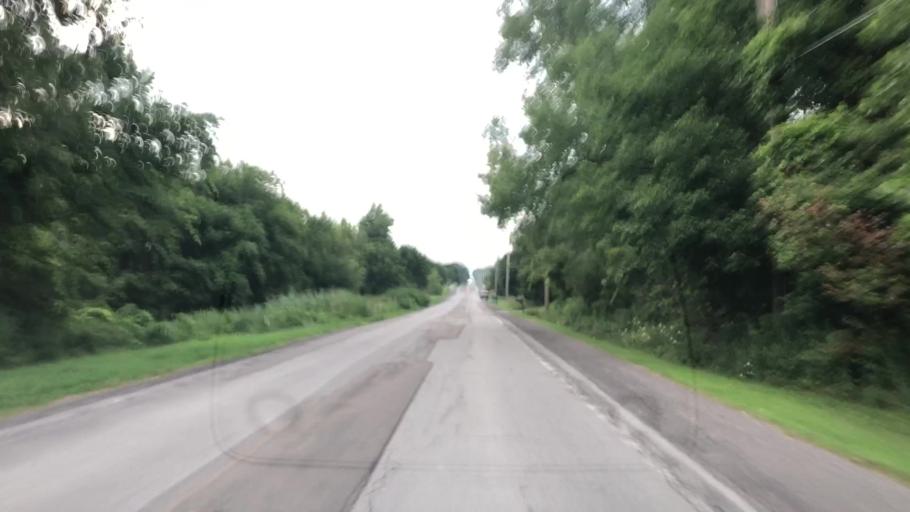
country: US
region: New York
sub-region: Erie County
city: Billington Heights
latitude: 42.7932
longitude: -78.6059
